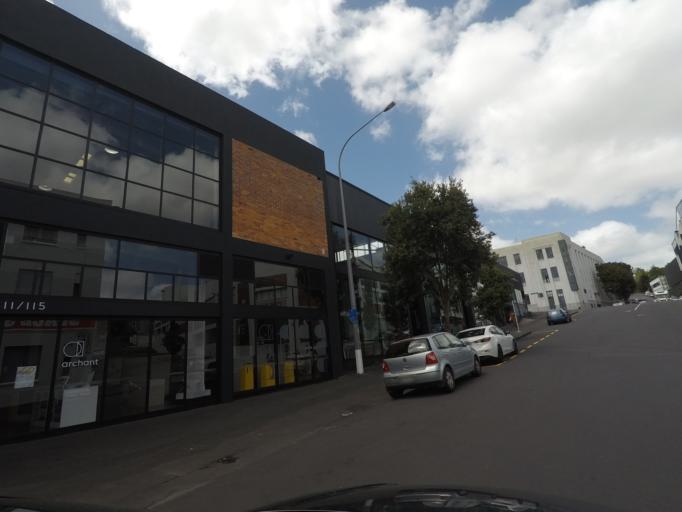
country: NZ
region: Auckland
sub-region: Auckland
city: Auckland
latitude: -36.8513
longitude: 174.7825
